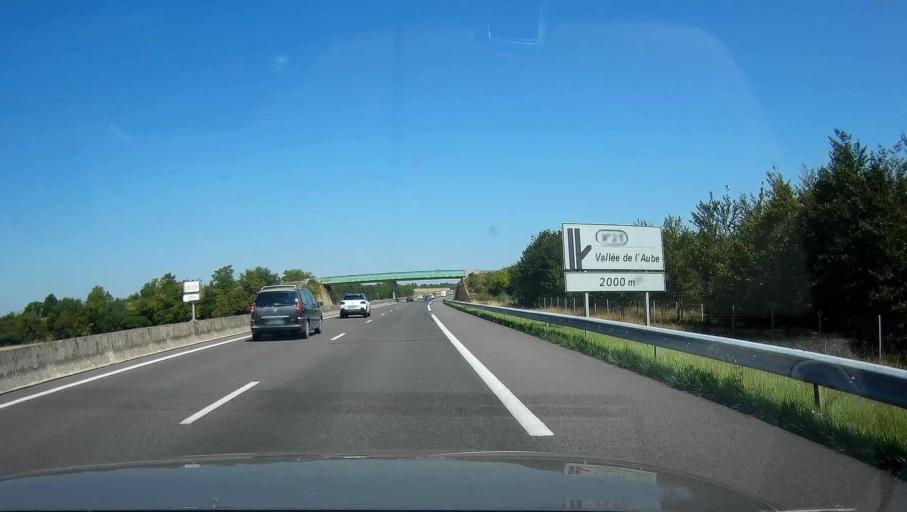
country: FR
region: Champagne-Ardenne
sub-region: Departement de l'Aube
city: Arcis-sur-Aube
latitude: 48.5055
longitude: 4.1675
